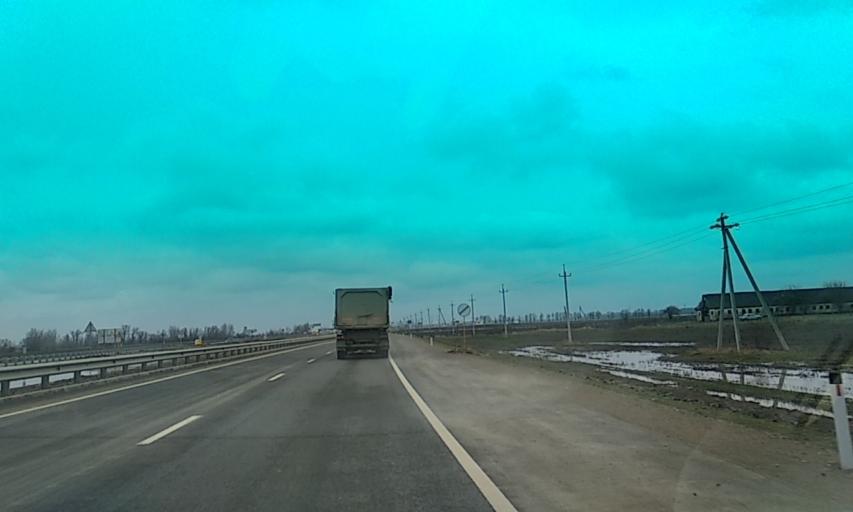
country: RU
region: Krasnodarskiy
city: Velikovechnoye
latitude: 44.9883
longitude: 39.7165
